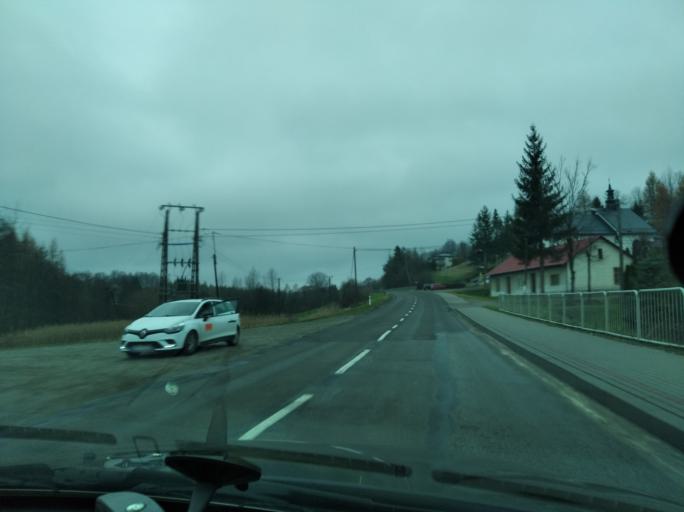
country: PL
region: Subcarpathian Voivodeship
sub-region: Powiat przeworski
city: Jawornik Polski
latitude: 49.8797
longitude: 22.2433
